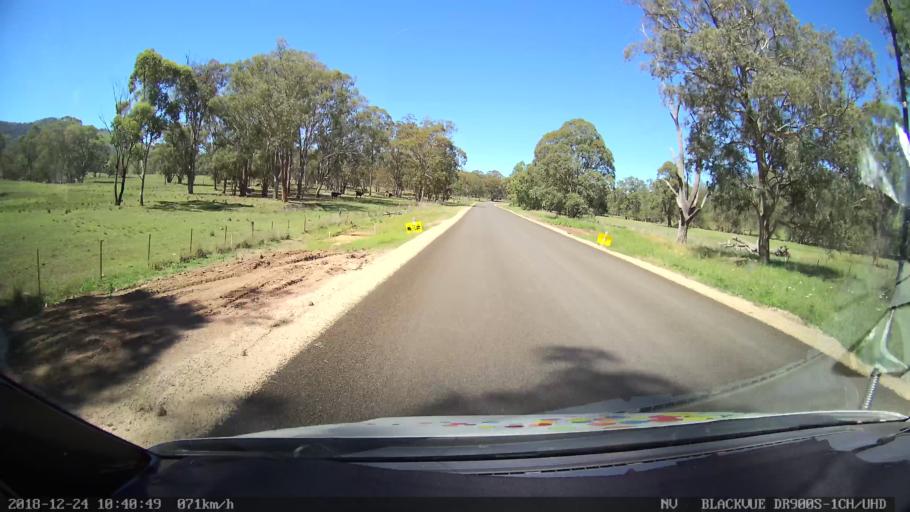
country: AU
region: New South Wales
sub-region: Upper Hunter Shire
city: Merriwa
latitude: -31.8645
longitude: 150.4642
